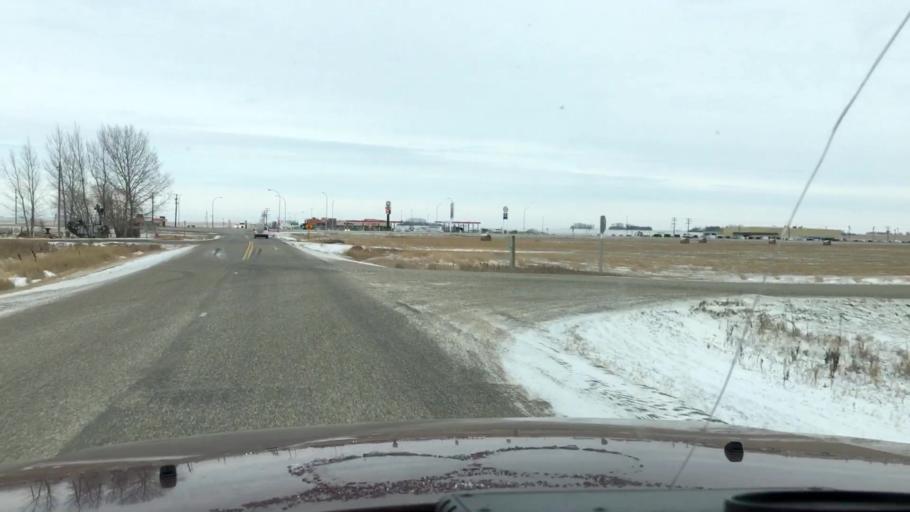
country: CA
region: Saskatchewan
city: Watrous
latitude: 51.2489
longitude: -105.9736
